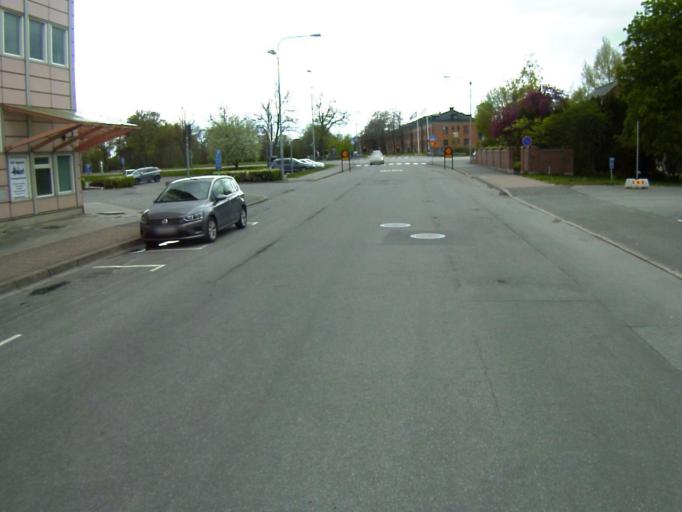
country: SE
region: Skane
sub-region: Kristianstads Kommun
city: Kristianstad
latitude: 56.0362
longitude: 14.1608
